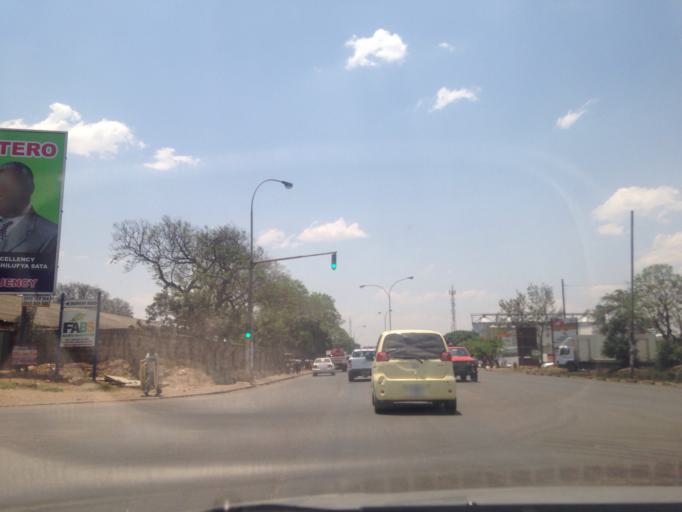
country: ZM
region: Lusaka
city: Lusaka
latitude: -15.4006
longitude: 28.2668
